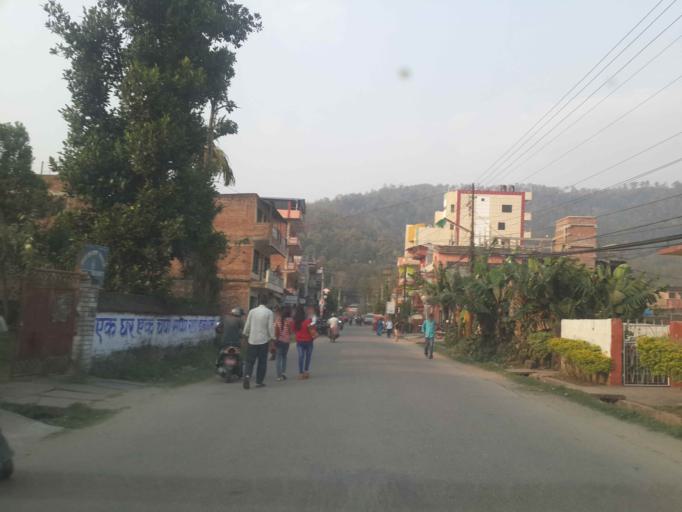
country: NP
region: Central Region
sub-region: Narayani Zone
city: Hitura
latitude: 27.4330
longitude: 85.0361
